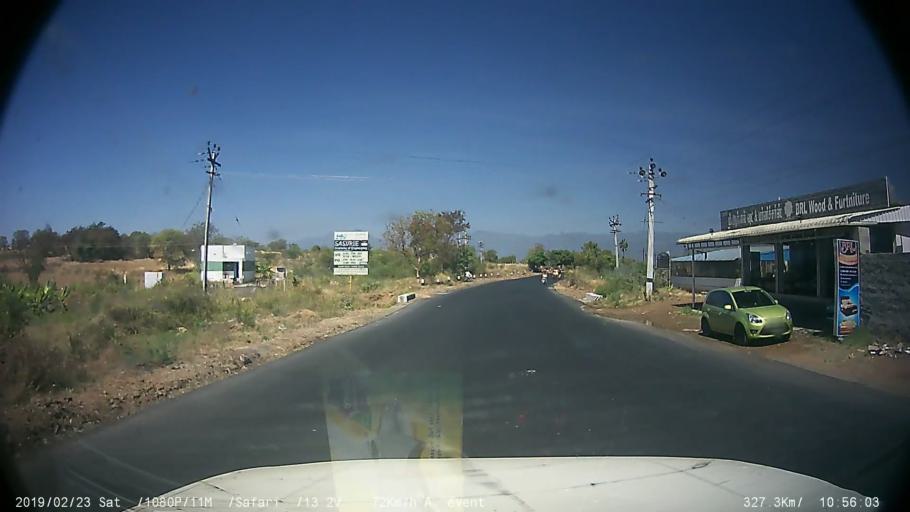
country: IN
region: Tamil Nadu
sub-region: Coimbatore
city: Sirumugai
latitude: 11.2601
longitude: 77.0331
